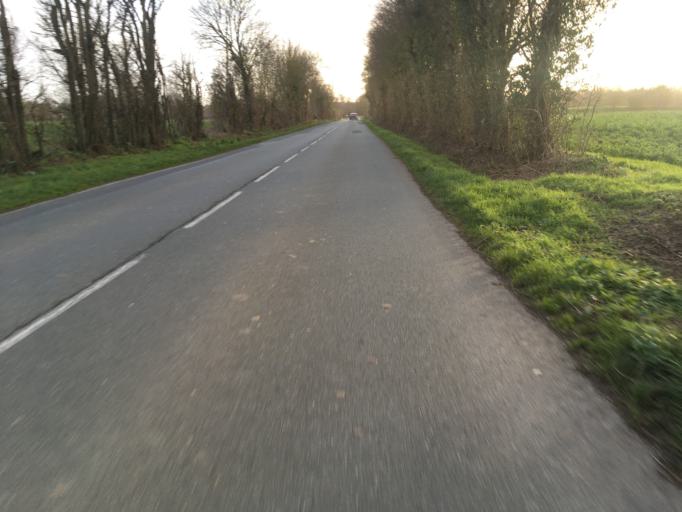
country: FR
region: Poitou-Charentes
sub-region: Departement de la Charente-Maritime
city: Courcon
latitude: 46.1725
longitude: -0.8479
